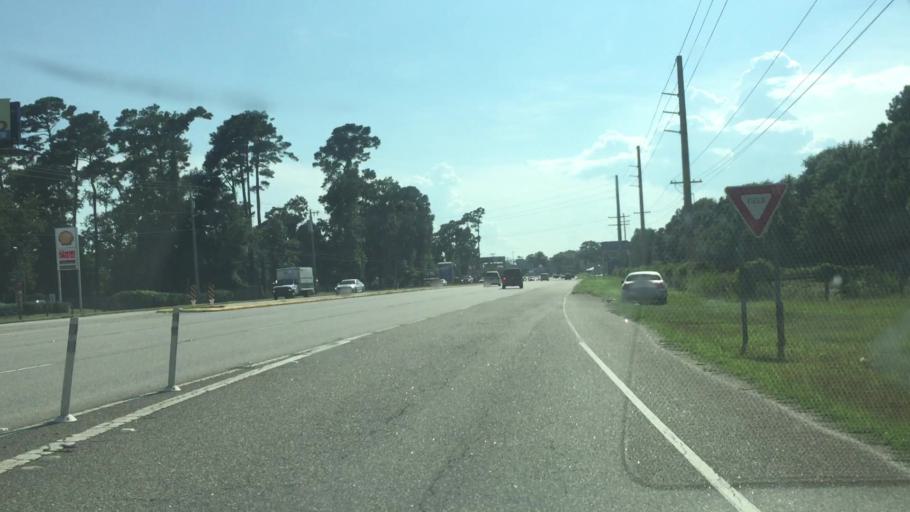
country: US
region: South Carolina
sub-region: Horry County
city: North Myrtle Beach
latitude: 33.7861
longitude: -78.7789
